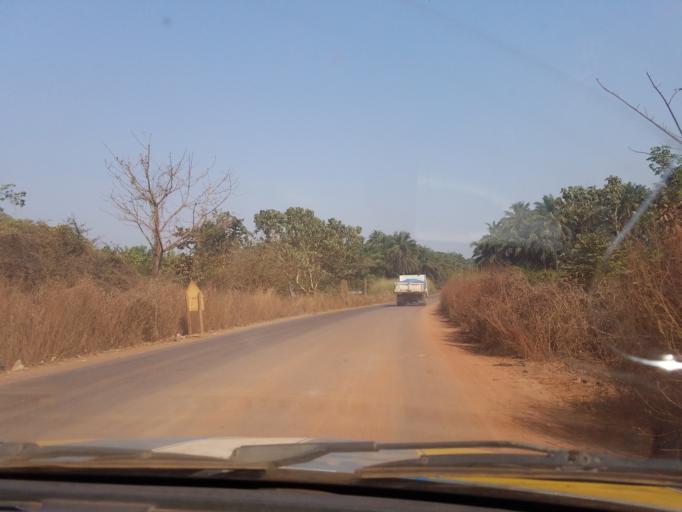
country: GN
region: Boke
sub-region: Boke Prefecture
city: Boke
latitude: 10.8345
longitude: -14.3626
